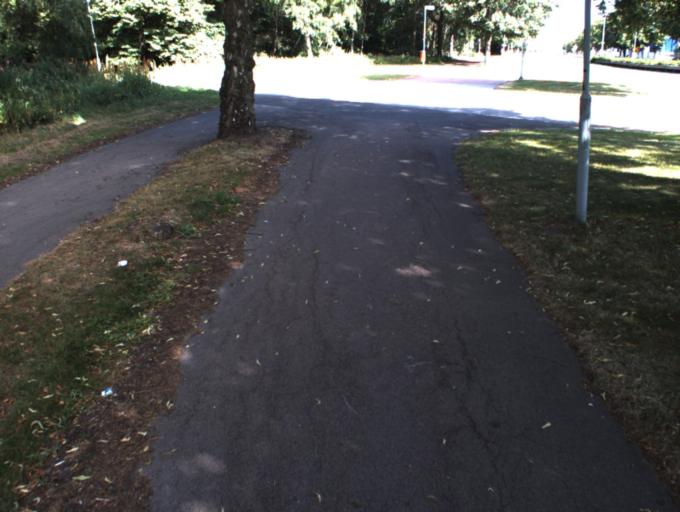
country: SE
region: Skane
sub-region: Helsingborg
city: Helsingborg
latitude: 56.0222
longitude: 12.7167
